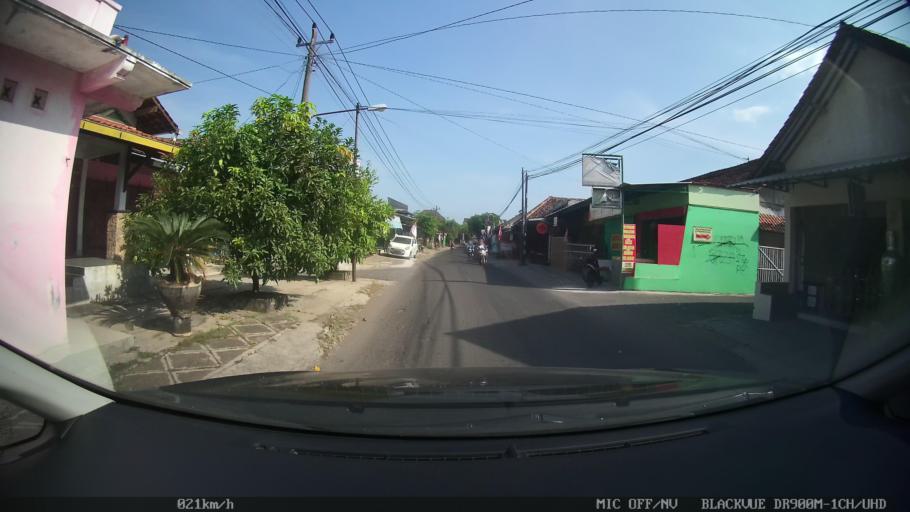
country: ID
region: Daerah Istimewa Yogyakarta
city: Kasihan
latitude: -7.8438
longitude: 110.3349
